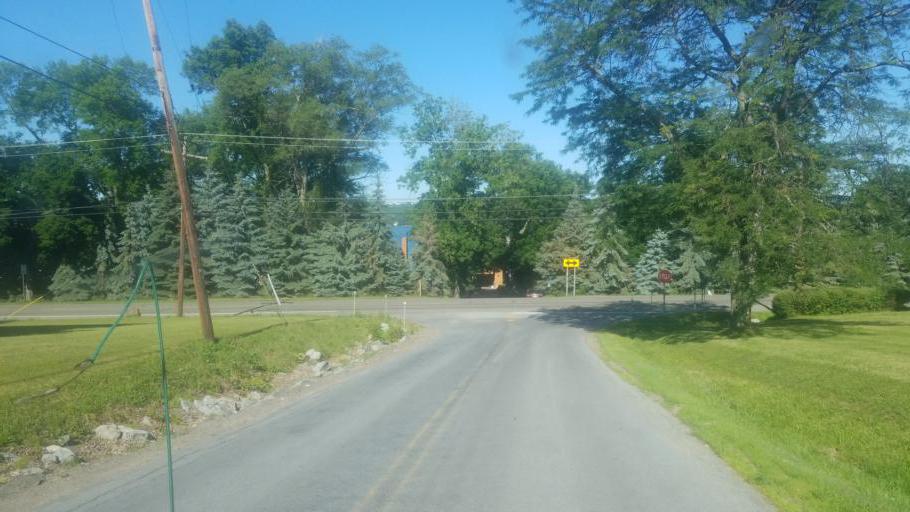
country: US
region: New York
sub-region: Ontario County
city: Canandaigua
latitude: 42.8397
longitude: -77.2551
